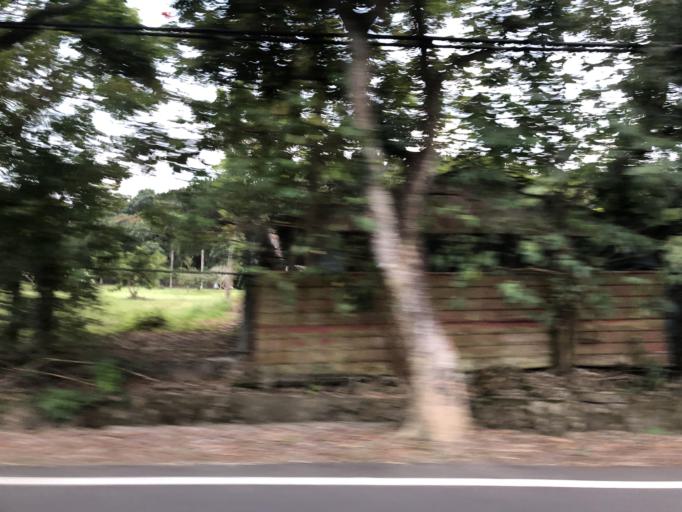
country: TW
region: Taiwan
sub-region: Tainan
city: Tainan
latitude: 23.0253
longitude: 120.3467
